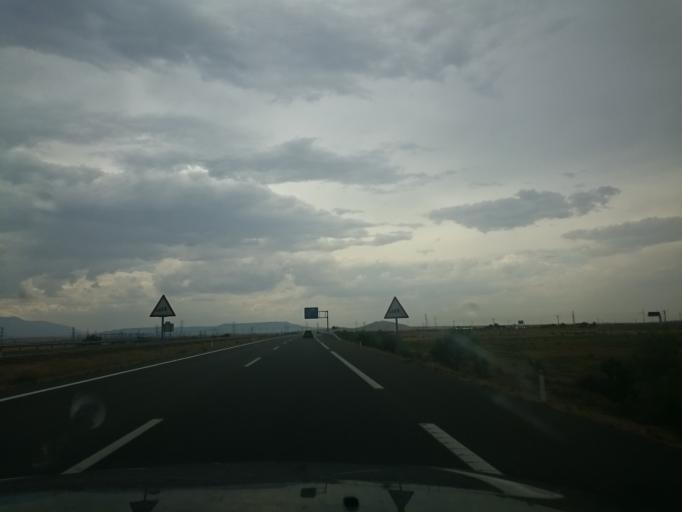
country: ES
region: Aragon
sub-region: Provincia de Zaragoza
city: Gallur
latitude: 41.8467
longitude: -1.3625
